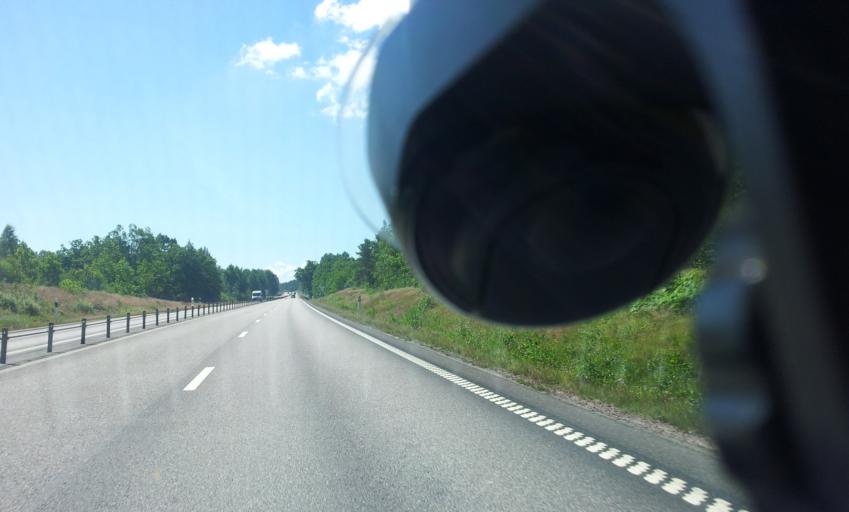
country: SE
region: Kalmar
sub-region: Oskarshamns Kommun
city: Paskallavik
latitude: 57.1453
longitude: 16.4687
